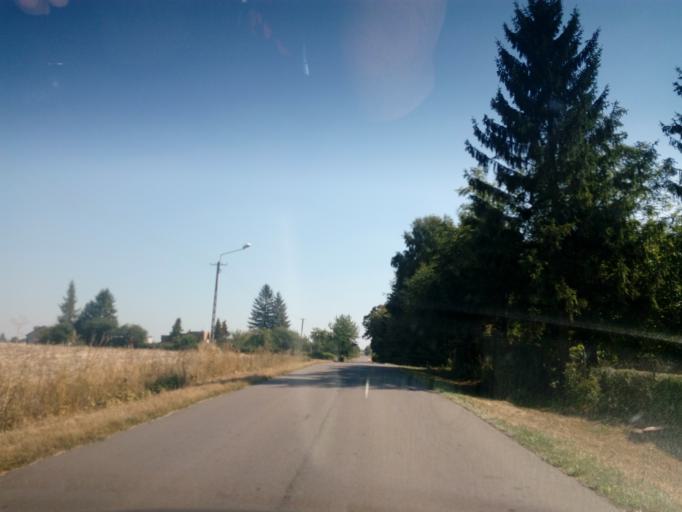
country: PL
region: Lublin Voivodeship
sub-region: Powiat hrubieszowski
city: Hrubieszow
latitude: 50.7292
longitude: 23.9228
